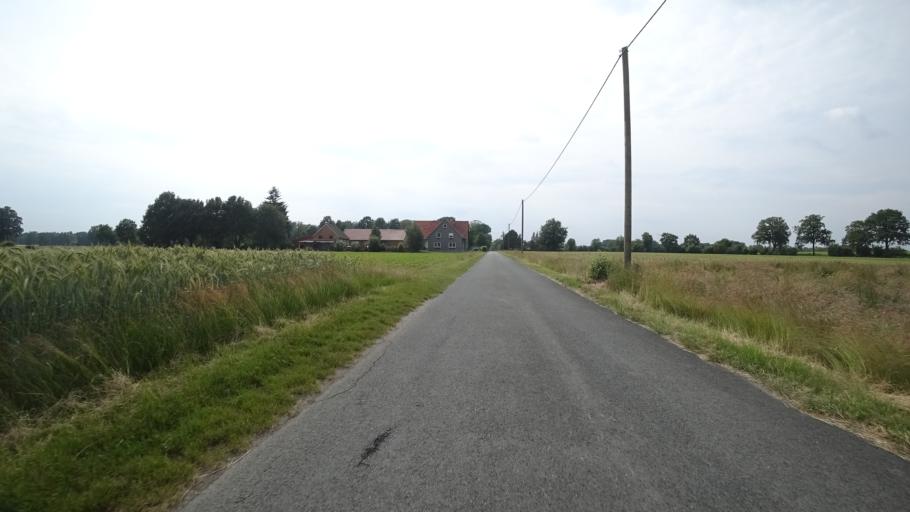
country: DE
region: North Rhine-Westphalia
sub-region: Regierungsbezirk Detmold
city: Guetersloh
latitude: 51.9497
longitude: 8.3592
